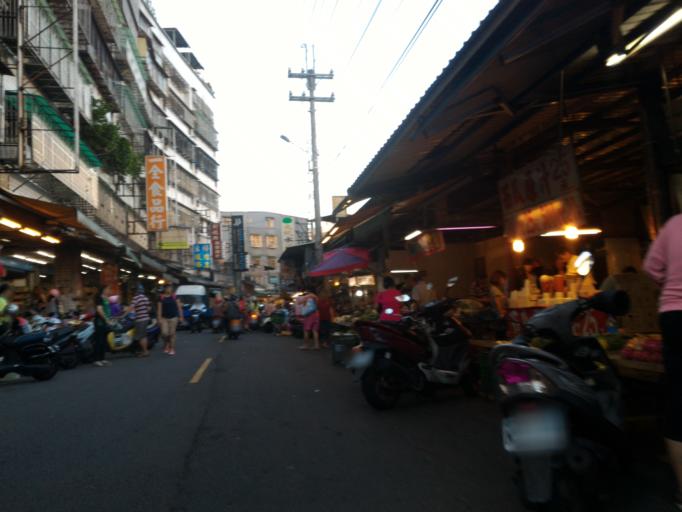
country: TW
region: Taipei
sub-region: Taipei
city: Banqiao
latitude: 24.9784
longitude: 121.4185
